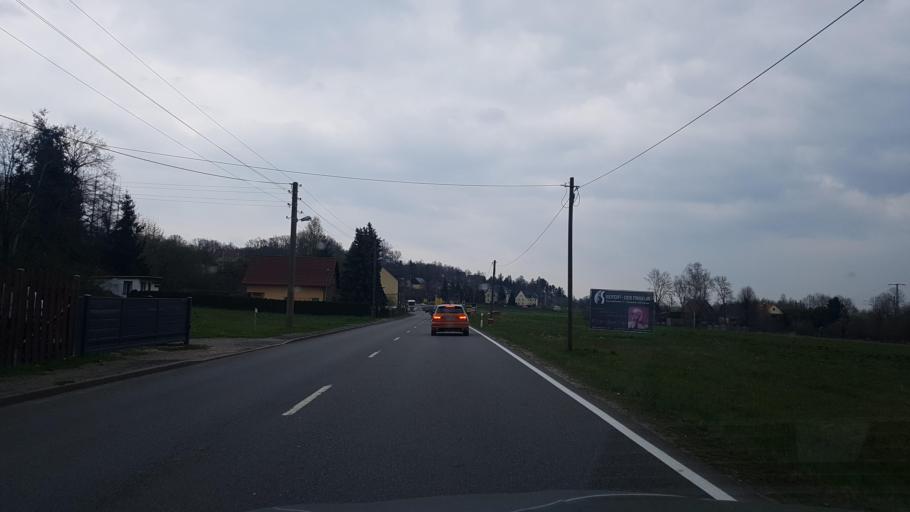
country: DE
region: Saxony
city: Dennheritz
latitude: 50.8132
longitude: 12.4899
